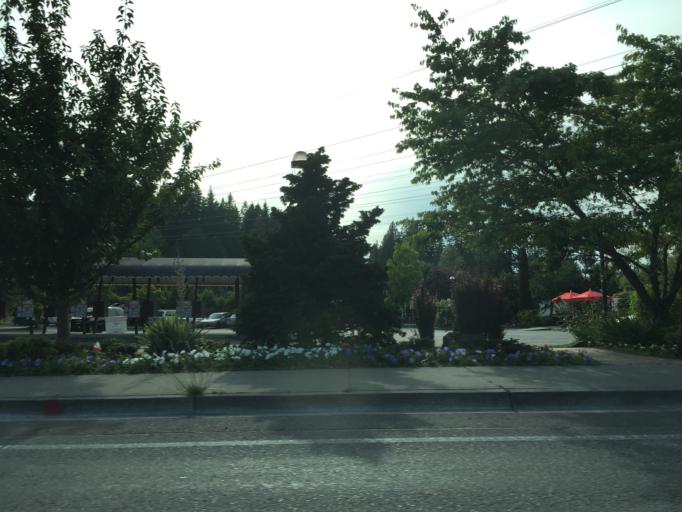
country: US
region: Washington
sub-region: Snohomish County
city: Mill Creek
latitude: 47.8290
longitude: -122.2092
